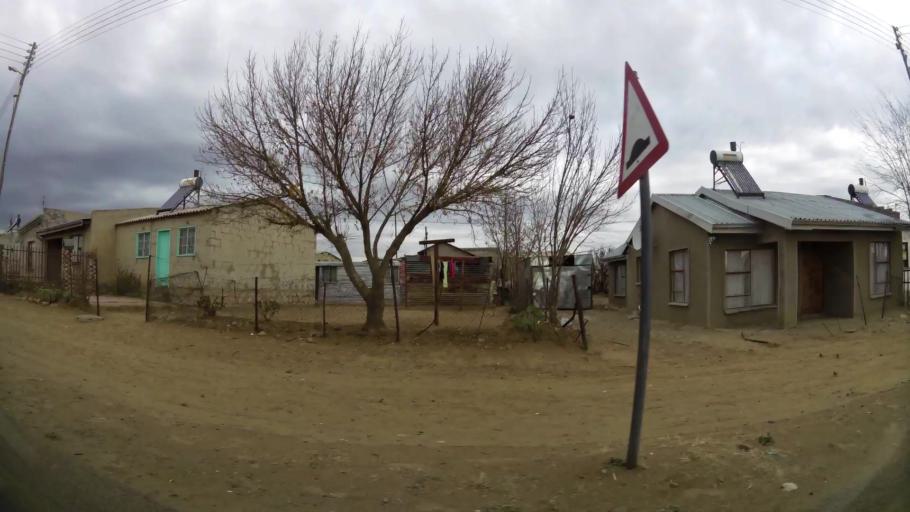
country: ZA
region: Orange Free State
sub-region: Fezile Dabi District Municipality
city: Kroonstad
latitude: -27.6430
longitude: 27.1850
